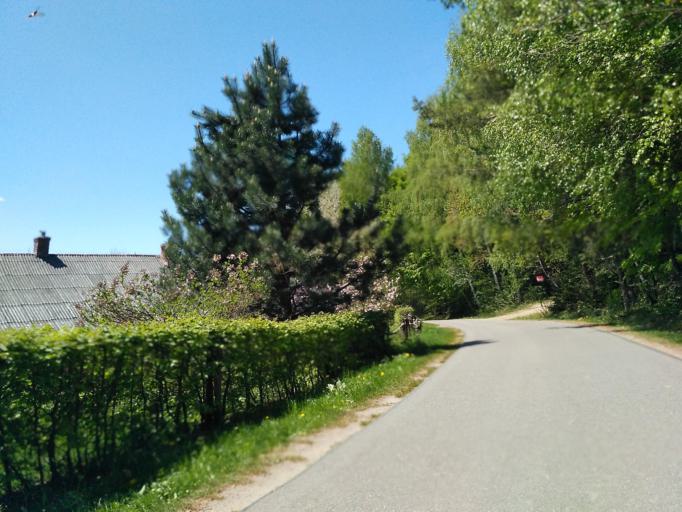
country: PL
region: Subcarpathian Voivodeship
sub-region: Powiat krosnienski
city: Korczyna
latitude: 49.7340
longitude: 21.8551
